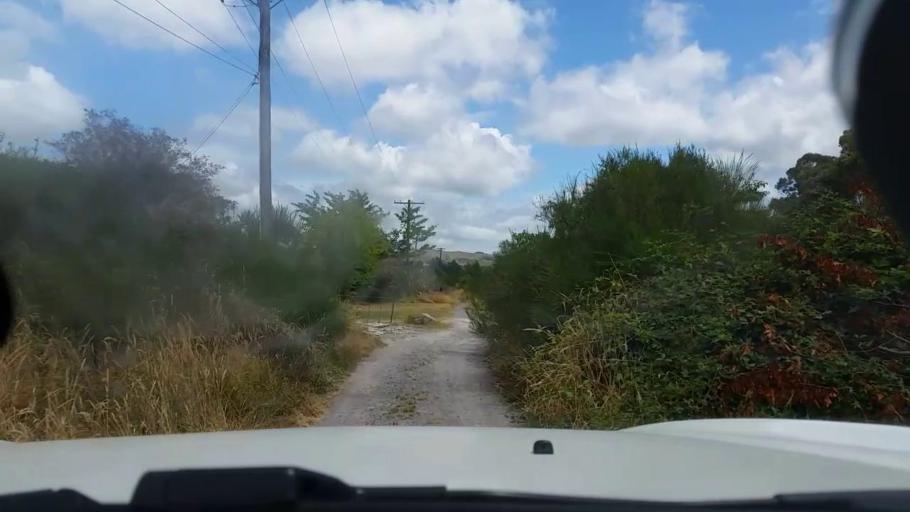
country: NZ
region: Bay of Plenty
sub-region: Rotorua District
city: Rotorua
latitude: -38.1453
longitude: 176.2701
